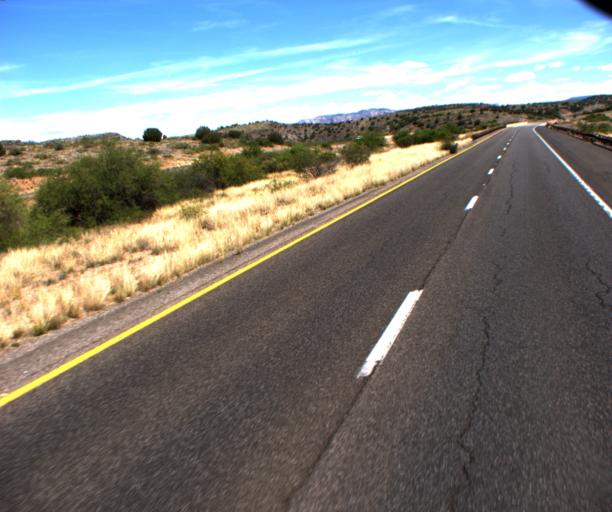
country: US
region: Arizona
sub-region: Yavapai County
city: Cornville
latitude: 34.7815
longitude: -111.9258
